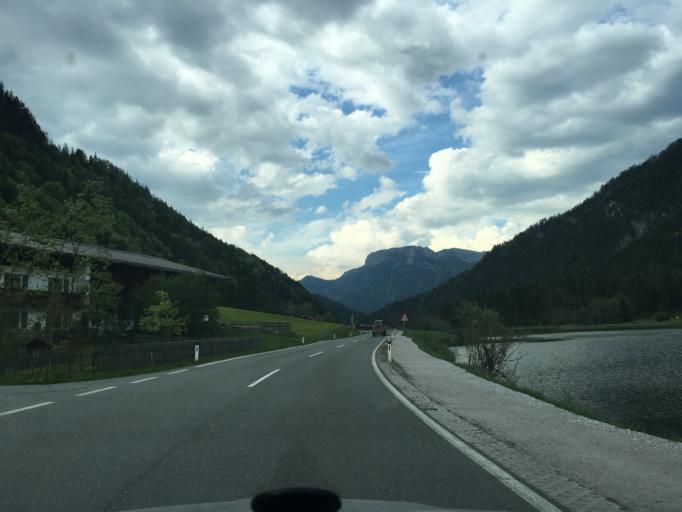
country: AT
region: Tyrol
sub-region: Politischer Bezirk Kitzbuhel
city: Waidring
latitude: 47.5372
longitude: 12.5679
